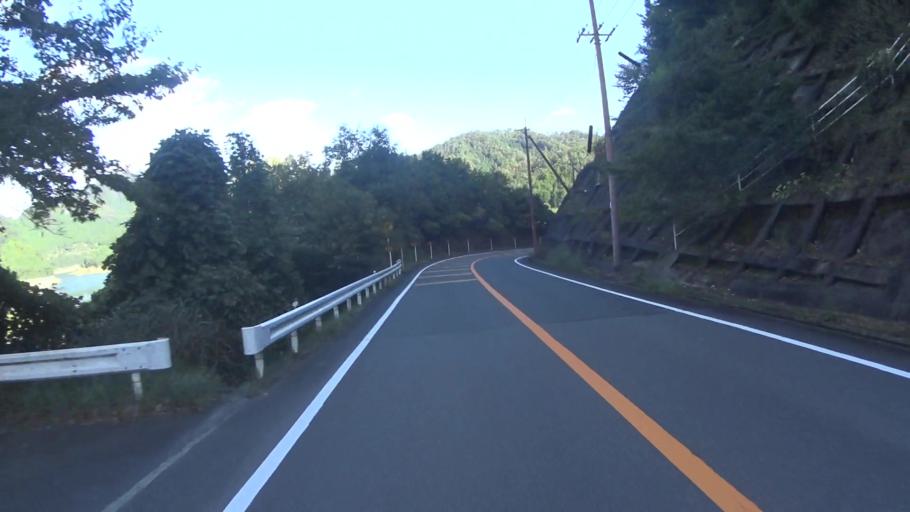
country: JP
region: Kyoto
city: Kameoka
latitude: 35.1318
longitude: 135.5393
